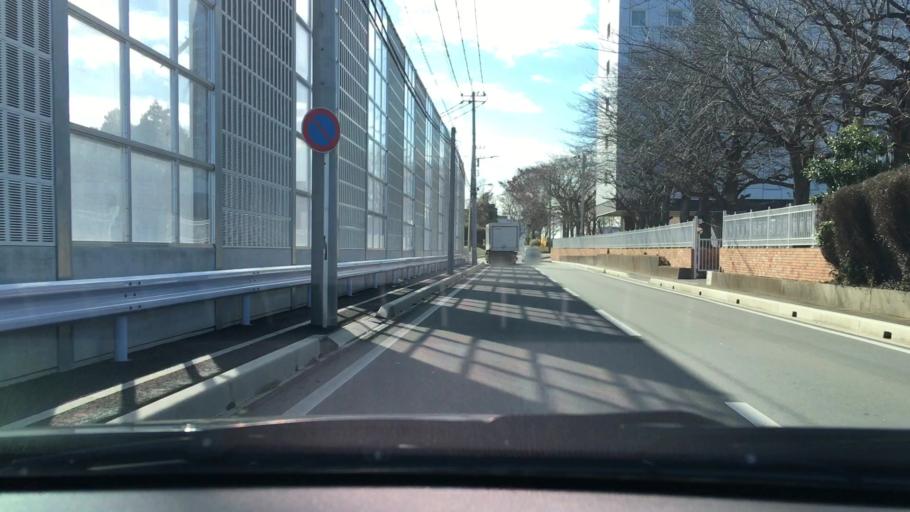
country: JP
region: Chiba
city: Narita
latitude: 35.7828
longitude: 140.3850
